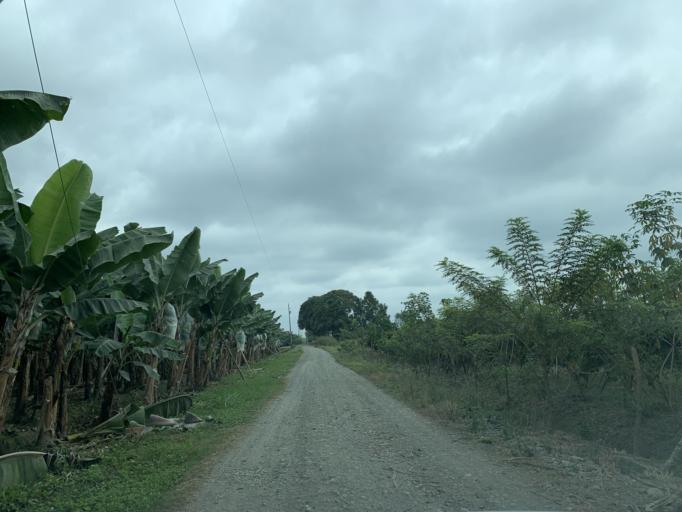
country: EC
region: Guayas
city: Coronel Marcelino Mariduena
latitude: -2.3426
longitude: -79.4581
